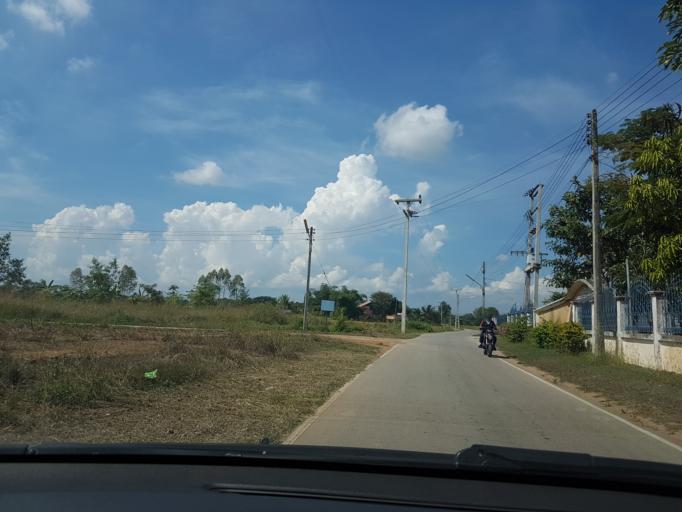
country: TH
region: Lampang
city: Ko Kha
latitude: 18.2093
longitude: 99.3976
